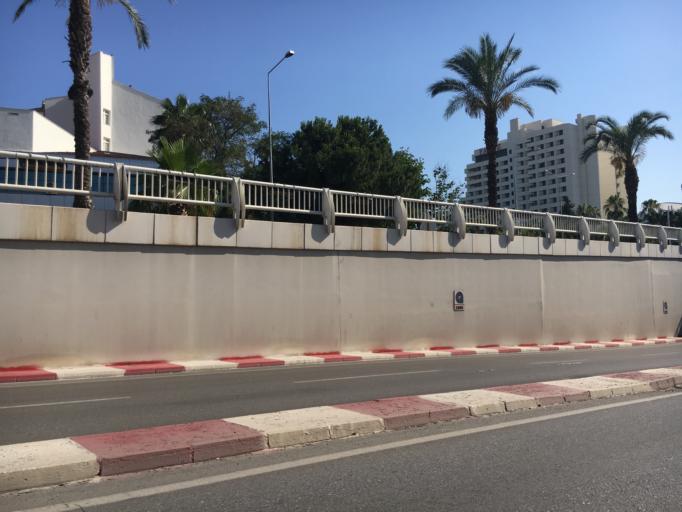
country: TR
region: Antalya
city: Antalya
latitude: 36.8881
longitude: 30.6785
